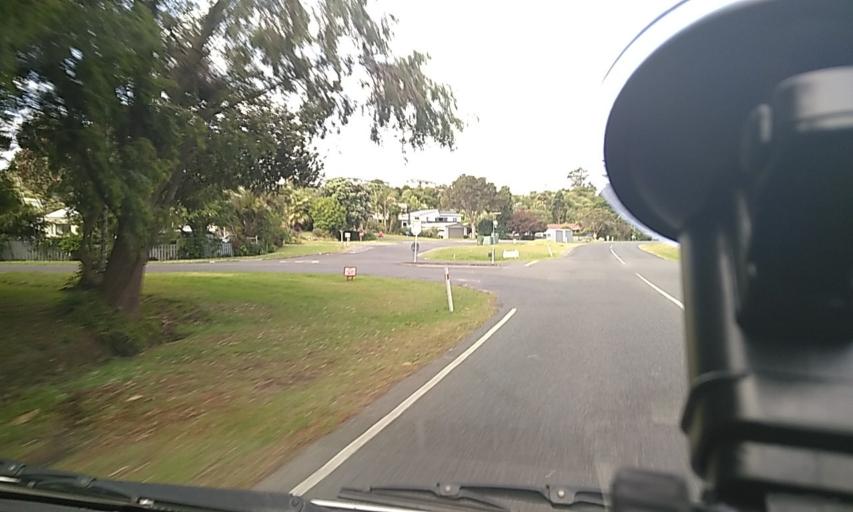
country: NZ
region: Bay of Plenty
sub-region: Western Bay of Plenty District
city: Waihi Beach
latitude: -37.4468
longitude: 175.9567
